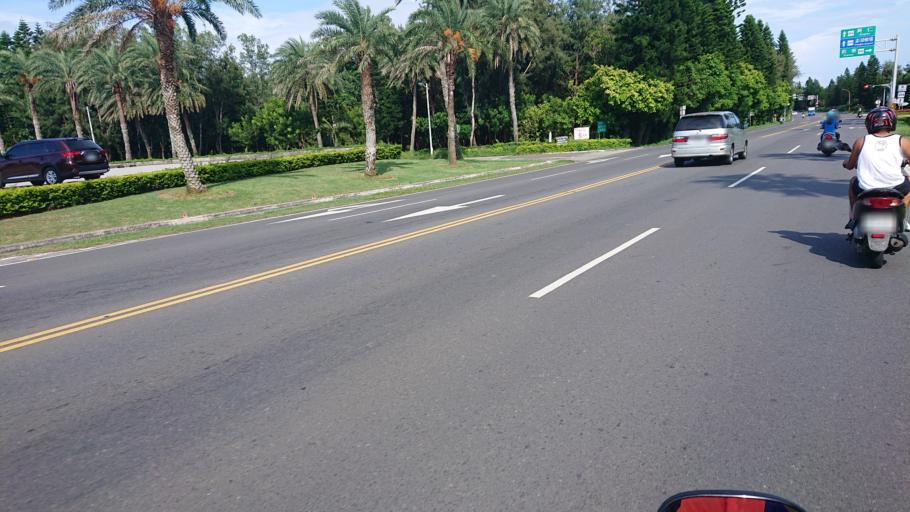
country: TW
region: Taiwan
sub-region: Penghu
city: Ma-kung
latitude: 23.5553
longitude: 119.6066
